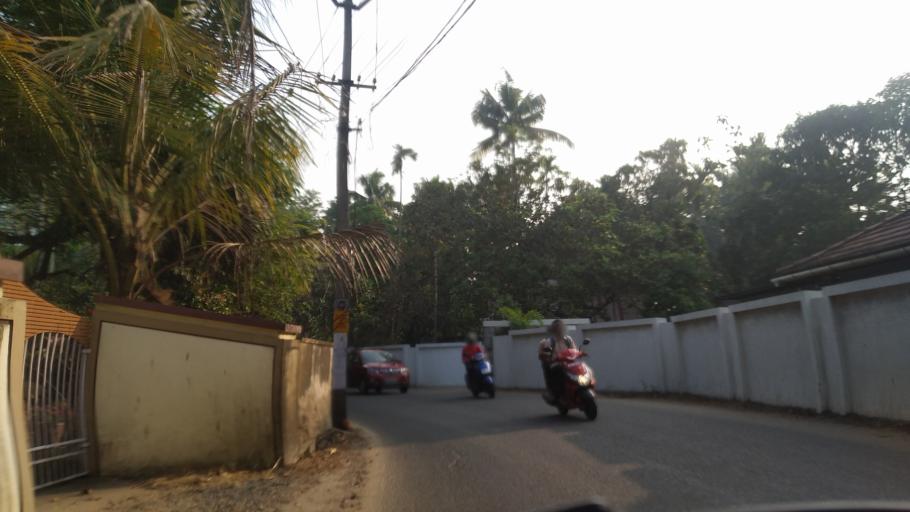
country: IN
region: Kerala
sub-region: Thrissur District
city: Kodungallur
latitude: 10.1878
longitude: 76.1999
